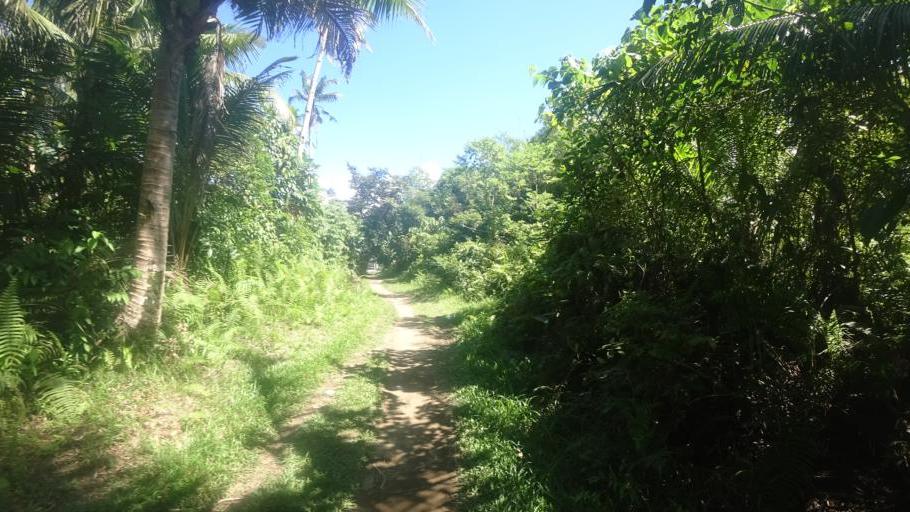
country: PH
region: Eastern Visayas
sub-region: Province of Leyte
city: Liberty
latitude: 10.8569
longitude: 124.9952
